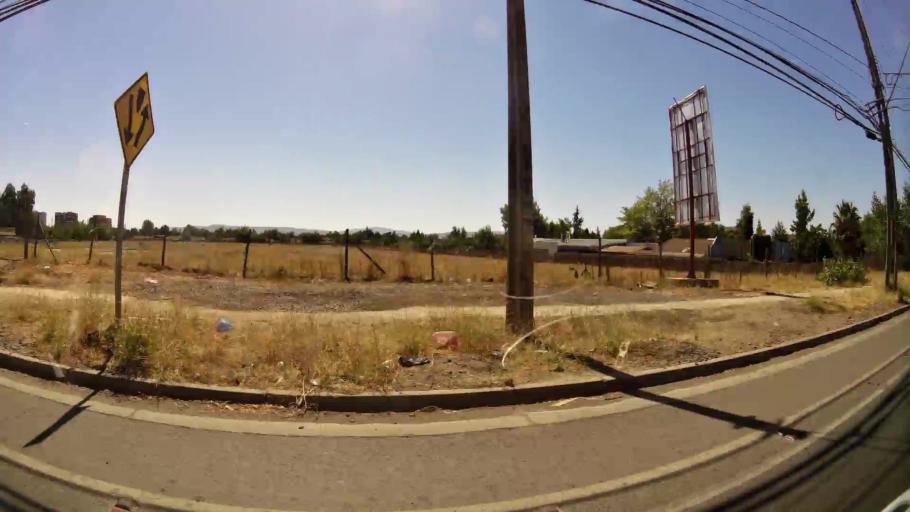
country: CL
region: Maule
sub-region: Provincia de Talca
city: Talca
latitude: -35.4357
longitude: -71.6101
